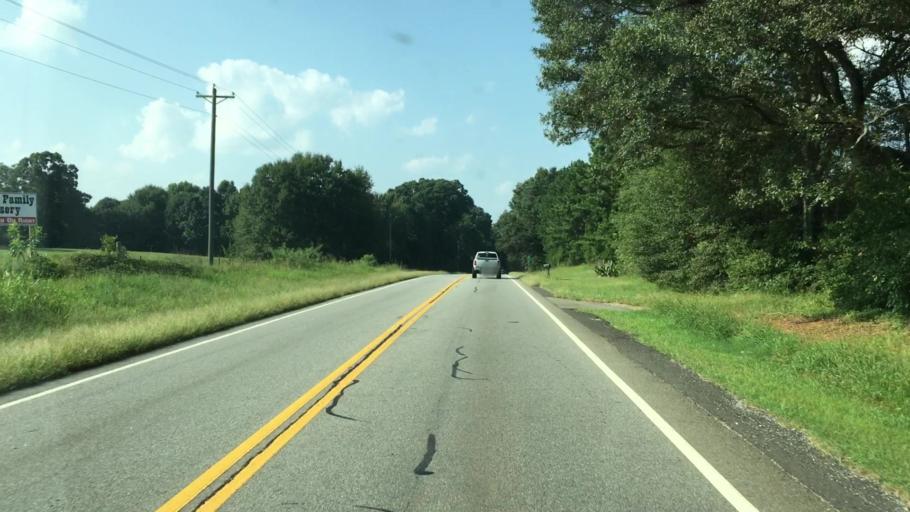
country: US
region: Georgia
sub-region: Walton County
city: Monroe
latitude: 33.8822
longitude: -83.7211
